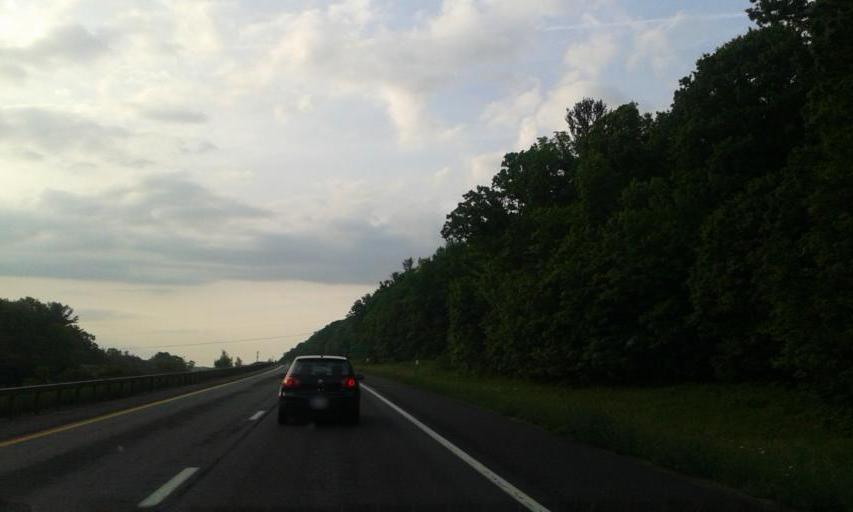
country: US
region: New York
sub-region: Broome County
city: Chenango Bridge
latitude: 42.1742
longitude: -75.8974
